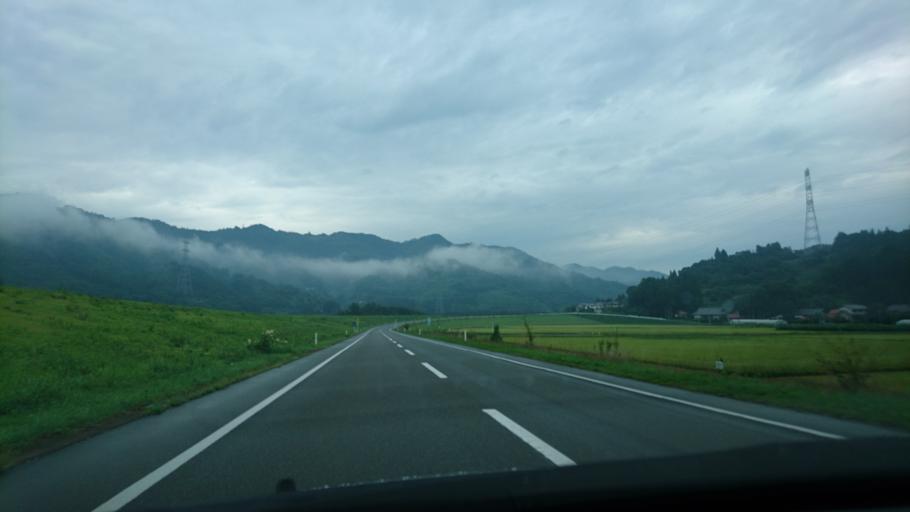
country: JP
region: Iwate
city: Ichinoseki
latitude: 38.9311
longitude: 141.2532
